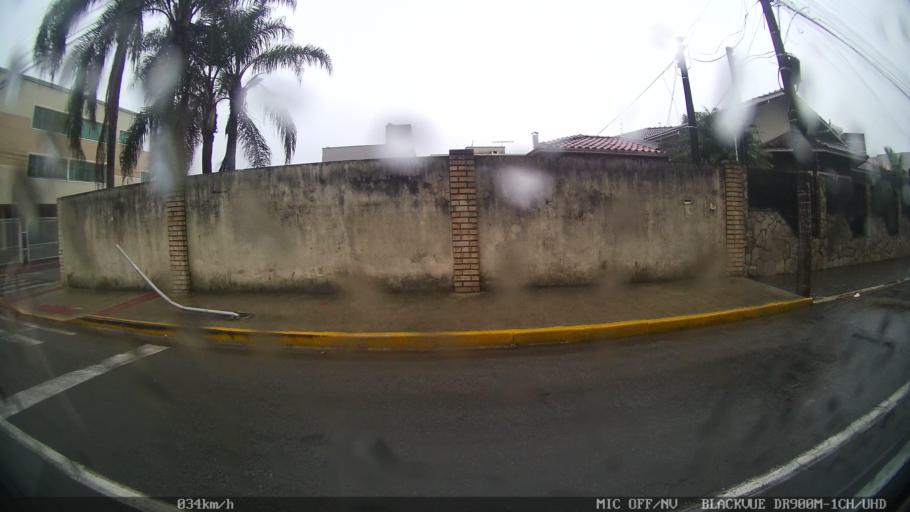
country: BR
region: Santa Catarina
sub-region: Itajai
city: Itajai
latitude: -26.9110
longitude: -48.6808
